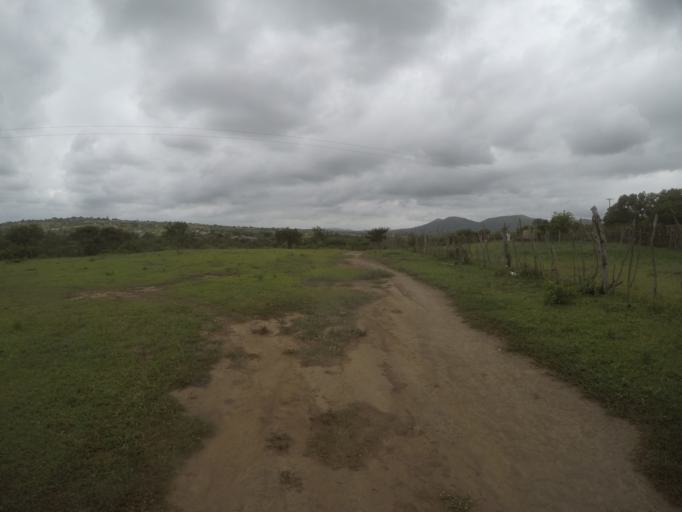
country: ZA
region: KwaZulu-Natal
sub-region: uThungulu District Municipality
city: Empangeni
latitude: -28.5912
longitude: 31.8440
